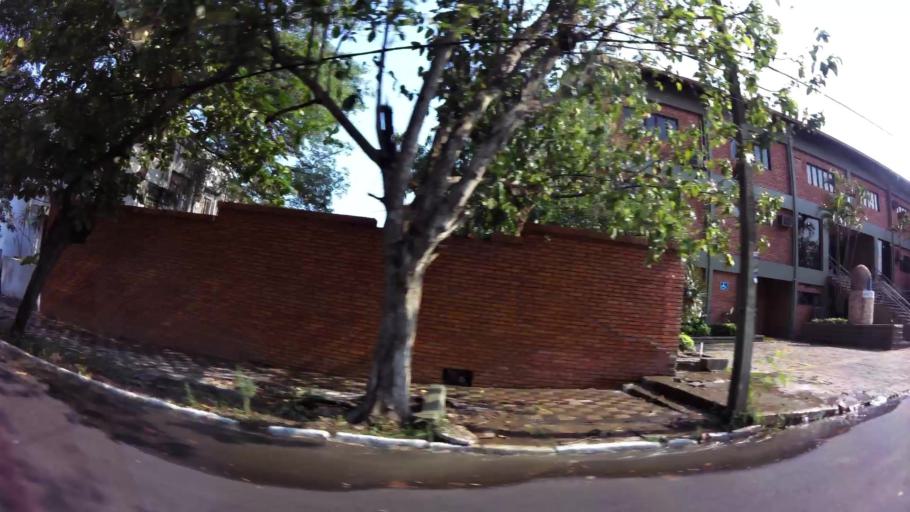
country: PY
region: Presidente Hayes
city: Nanawa
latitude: -25.2909
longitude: -57.6675
